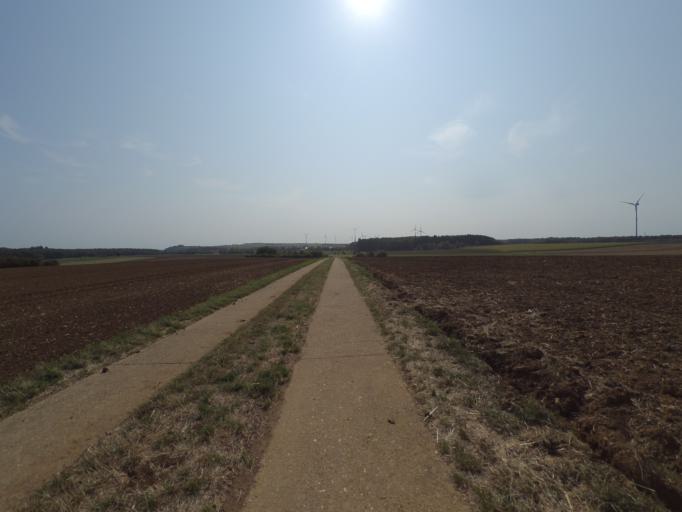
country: DE
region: Saarland
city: Orscholz
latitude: 49.4773
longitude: 6.4592
